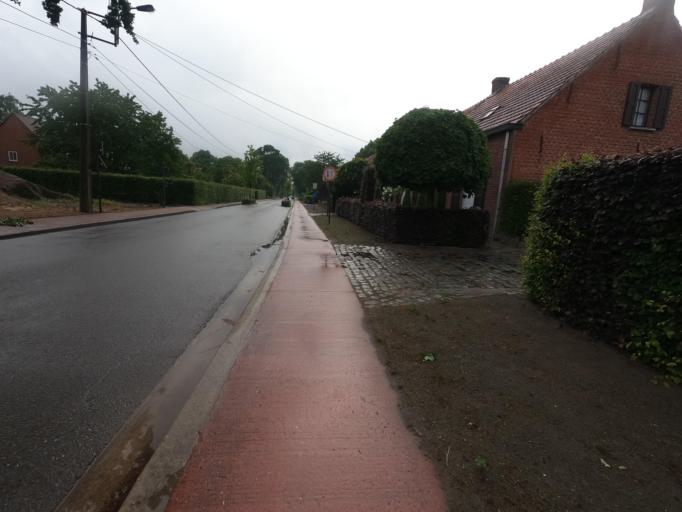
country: BE
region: Flanders
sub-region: Provincie Antwerpen
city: Kalmthout
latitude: 51.3745
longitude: 4.5182
